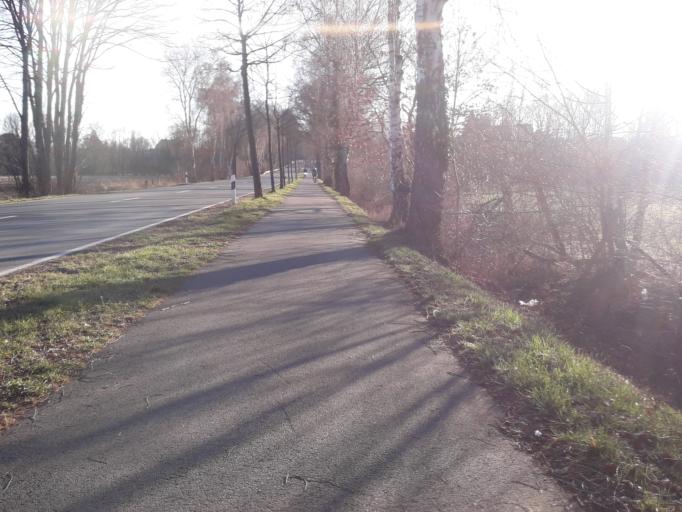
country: DE
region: North Rhine-Westphalia
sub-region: Regierungsbezirk Detmold
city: Paderborn
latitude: 51.6942
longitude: 8.7062
